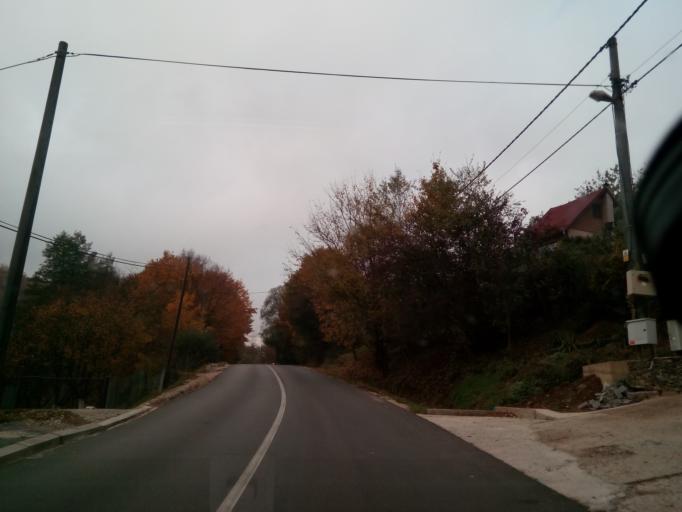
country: SK
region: Kosicky
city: Kosice
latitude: 48.7246
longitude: 21.1565
